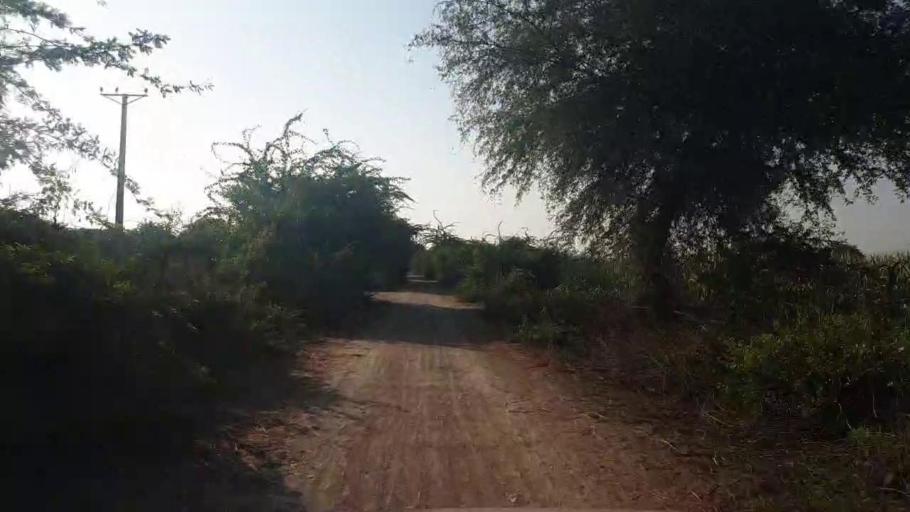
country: PK
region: Sindh
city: Badin
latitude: 24.7339
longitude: 68.8788
